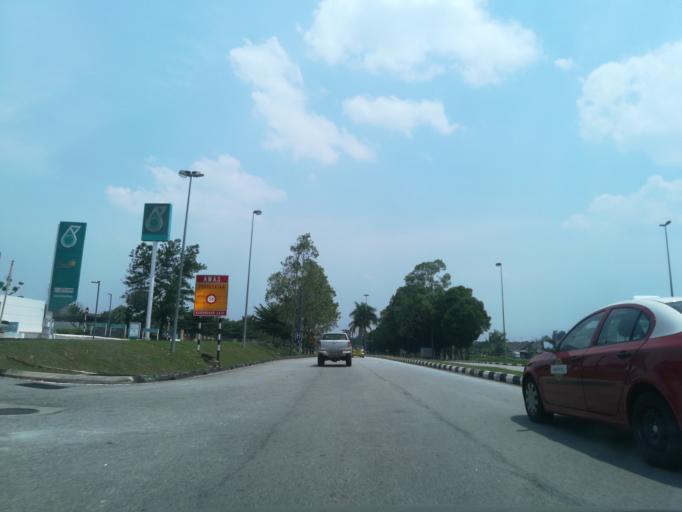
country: MY
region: Kedah
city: Kulim
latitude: 5.3951
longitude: 100.5736
